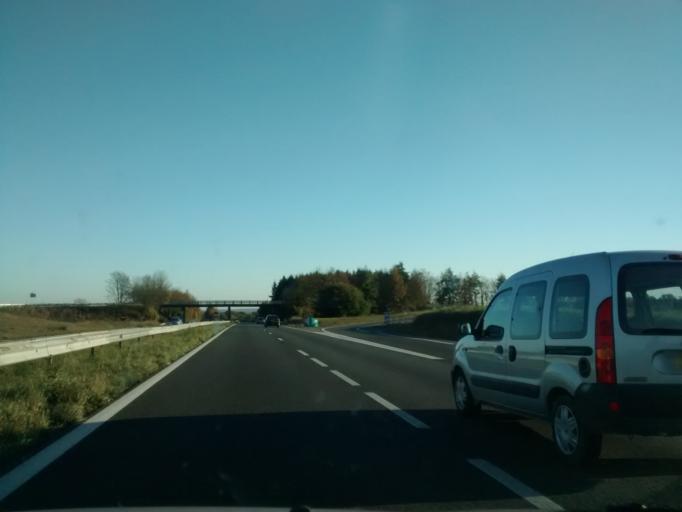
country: FR
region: Brittany
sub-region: Departement d'Ille-et-Vilaine
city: Montauban-de-Bretagne
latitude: 48.1977
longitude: -2.0277
